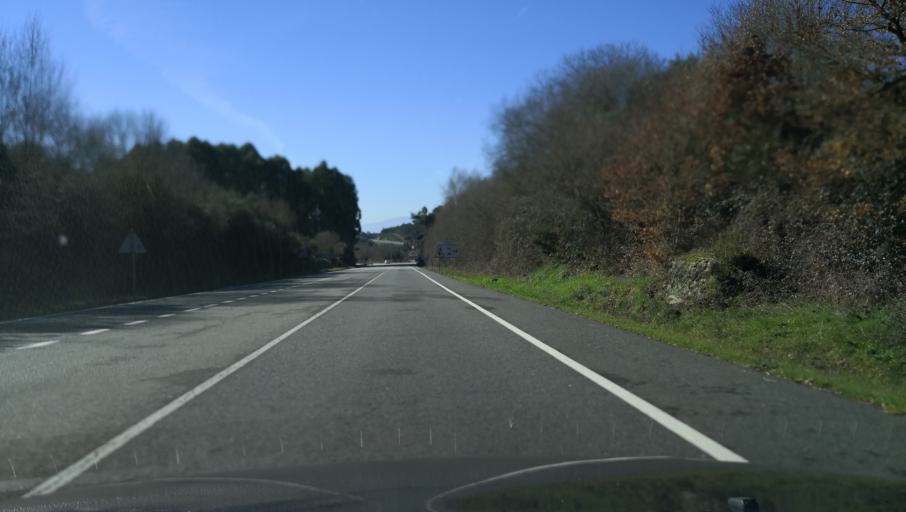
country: ES
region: Galicia
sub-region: Provincia de Ourense
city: Pinor
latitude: 42.5161
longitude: -8.0156
